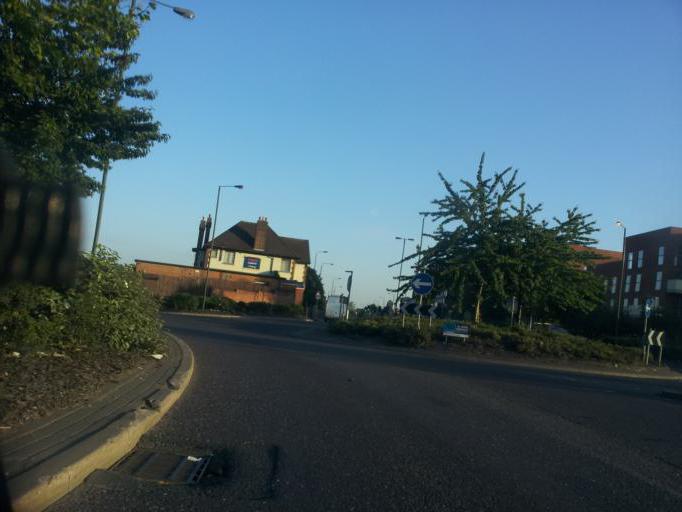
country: GB
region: England
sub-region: Greater London
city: Erith
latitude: 51.4740
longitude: 0.1815
